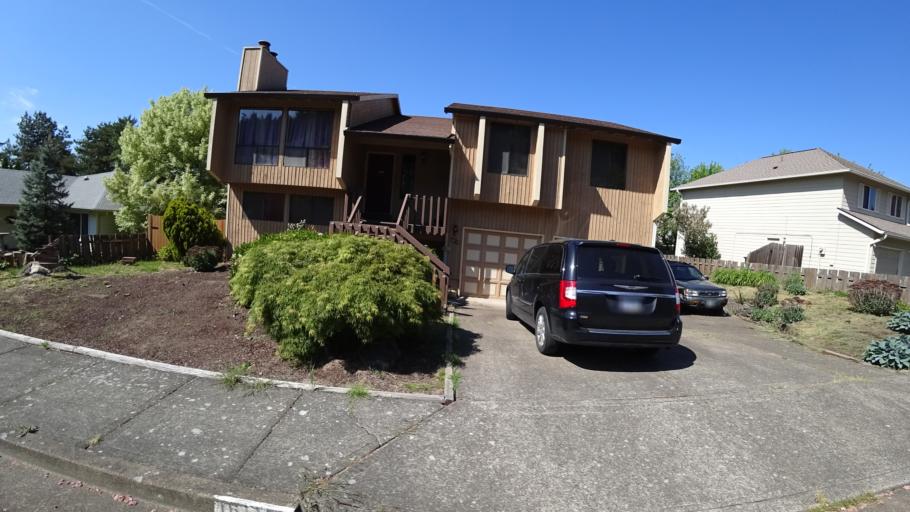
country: US
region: Oregon
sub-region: Washington County
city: Aloha
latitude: 45.4761
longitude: -122.8439
